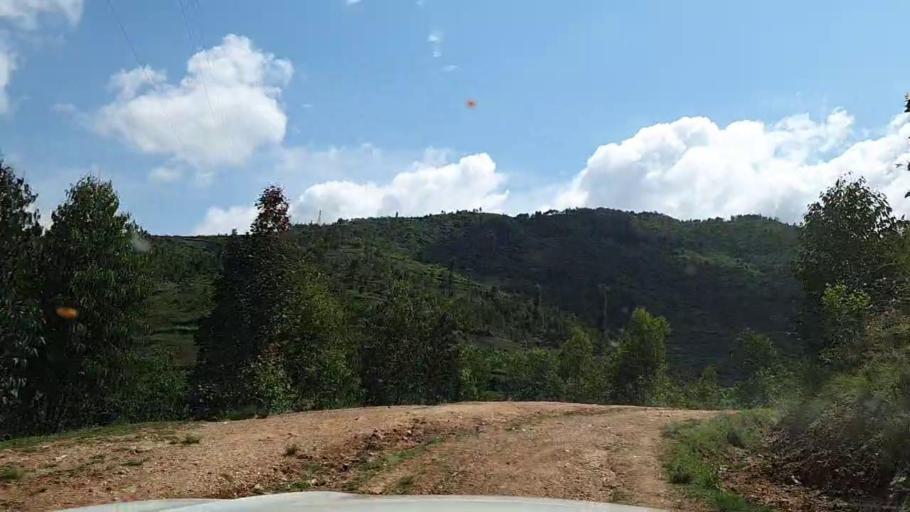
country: RW
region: Southern Province
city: Gikongoro
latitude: -2.3605
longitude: 29.5352
